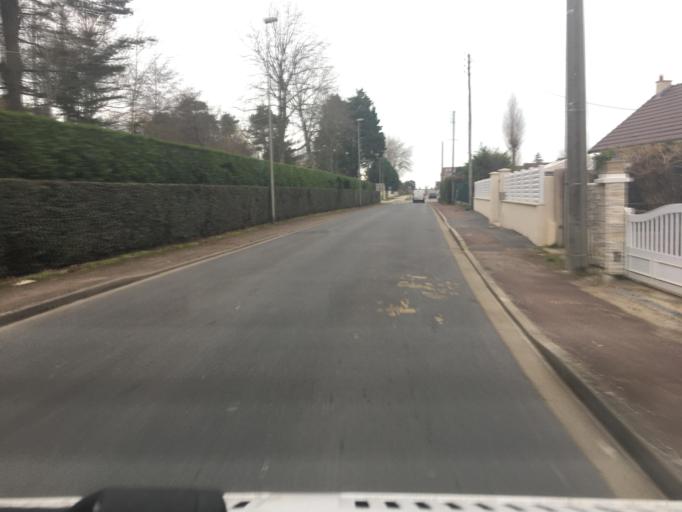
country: FR
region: Lower Normandy
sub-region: Departement du Calvados
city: Cabourg
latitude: 49.2845
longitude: -0.1395
